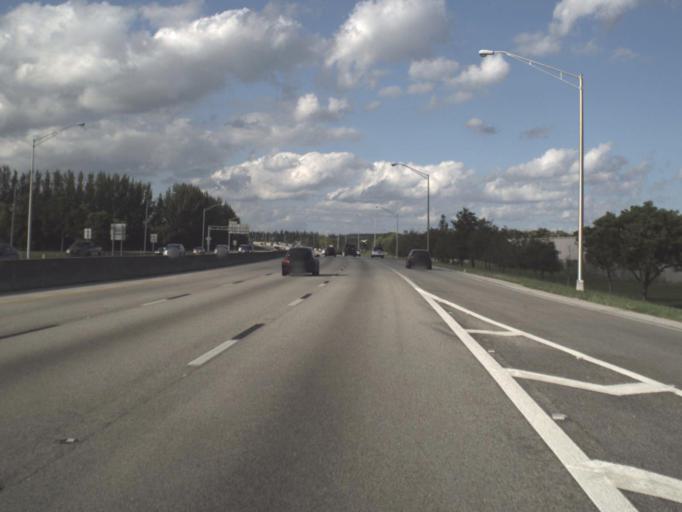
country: US
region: Florida
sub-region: Broward County
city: Coconut Creek
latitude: 26.2505
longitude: -80.1663
